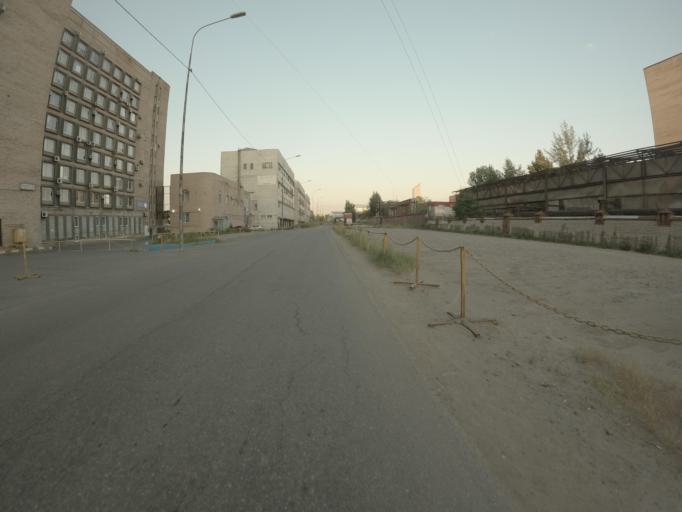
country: RU
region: St.-Petersburg
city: Admiralteisky
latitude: 59.8866
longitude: 30.2876
